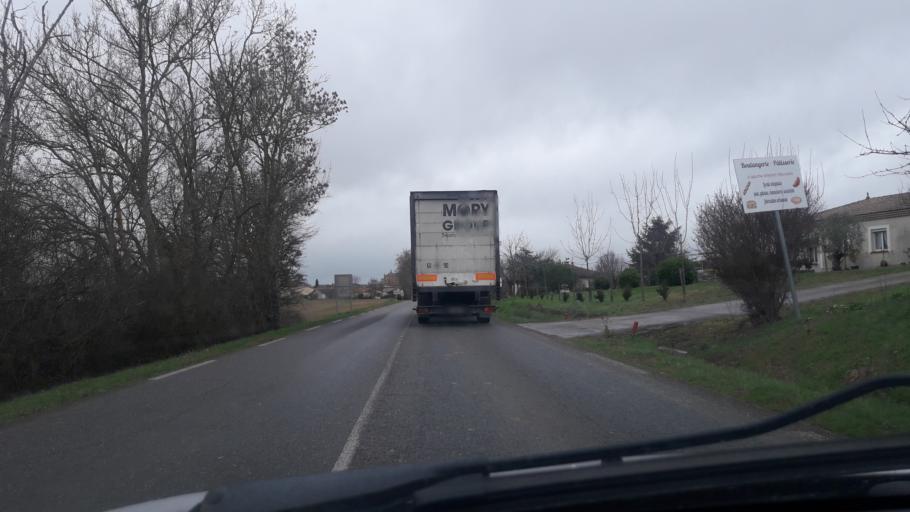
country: FR
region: Midi-Pyrenees
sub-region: Departement du Gers
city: Gimont
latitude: 43.7164
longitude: 0.9835
